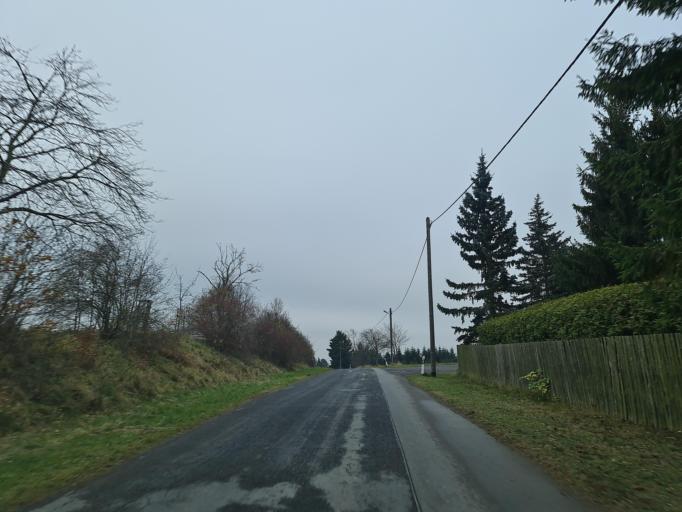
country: DE
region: Saxony
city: Mehltheuer
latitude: 50.5149
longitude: 12.0464
